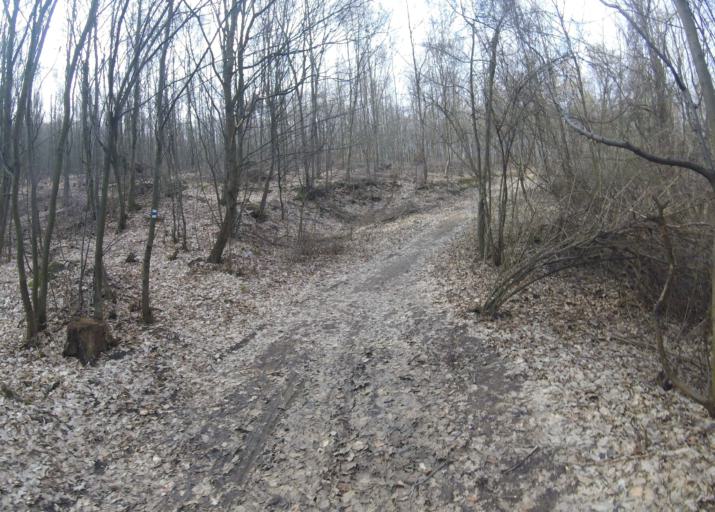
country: HU
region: Heves
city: Belapatfalva
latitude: 48.0415
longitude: 20.3591
